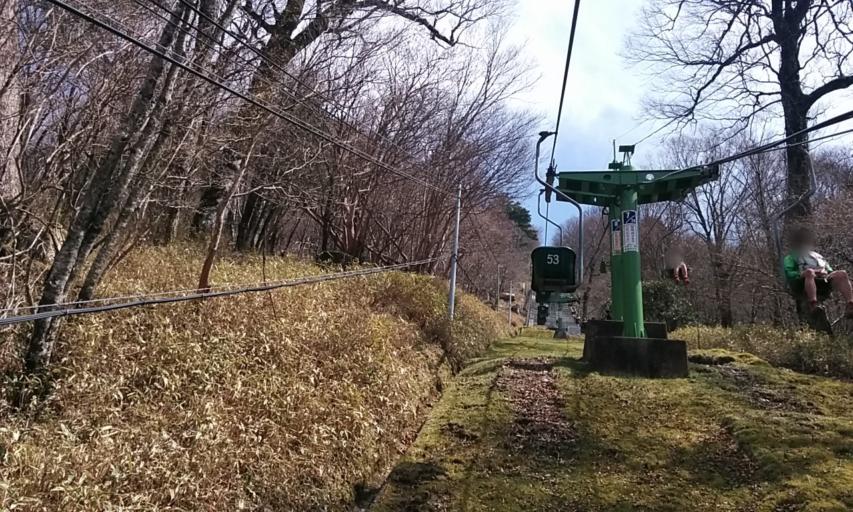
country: JP
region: Tokushima
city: Wakimachi
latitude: 33.8653
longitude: 134.0897
